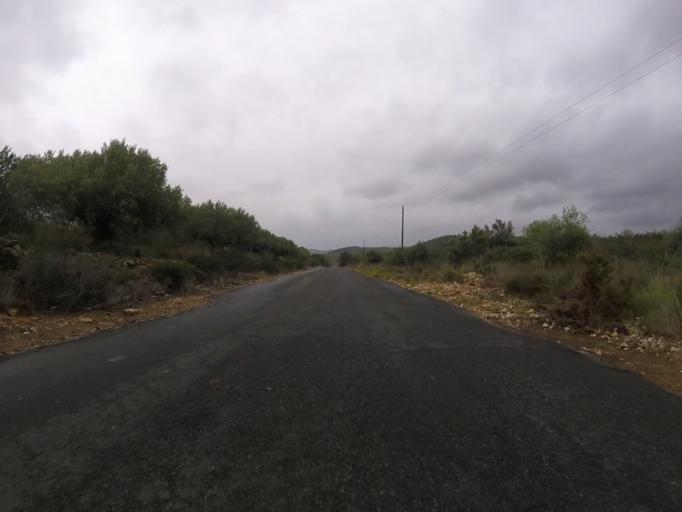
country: ES
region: Valencia
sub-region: Provincia de Castello
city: Alcala de Xivert
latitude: 40.2796
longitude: 0.2260
